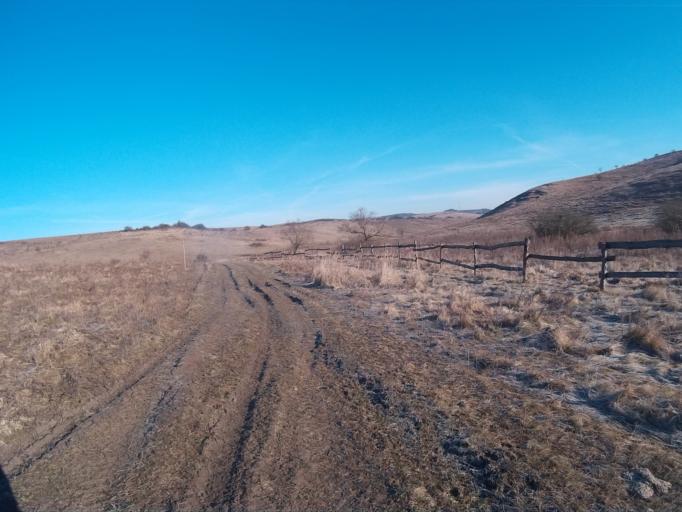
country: HU
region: Borsod-Abauj-Zemplen
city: Putnok
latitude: 48.3846
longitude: 20.4672
